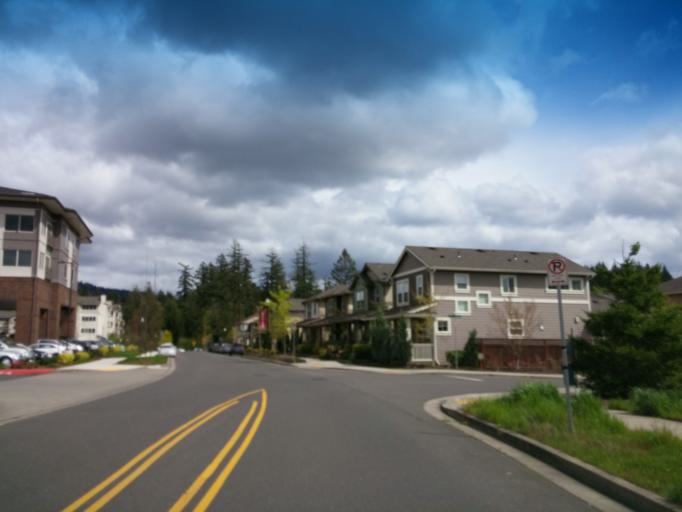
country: US
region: Oregon
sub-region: Washington County
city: Cedar Mill
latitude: 45.5208
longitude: -122.7998
